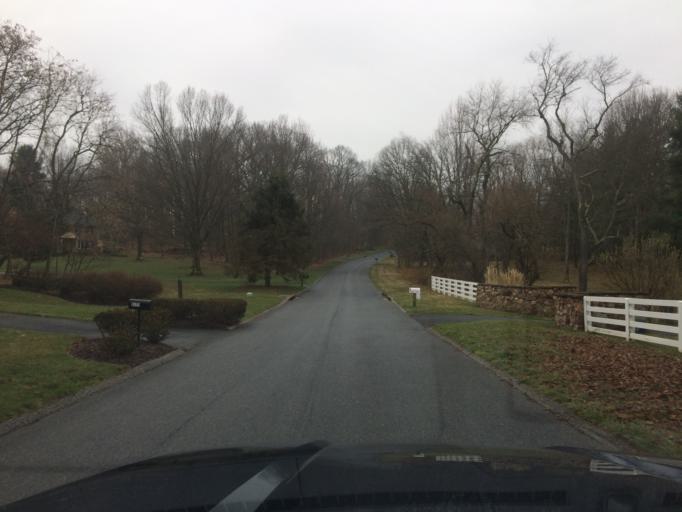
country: US
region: Maryland
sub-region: Carroll County
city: Sykesville
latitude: 39.2934
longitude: -77.0017
